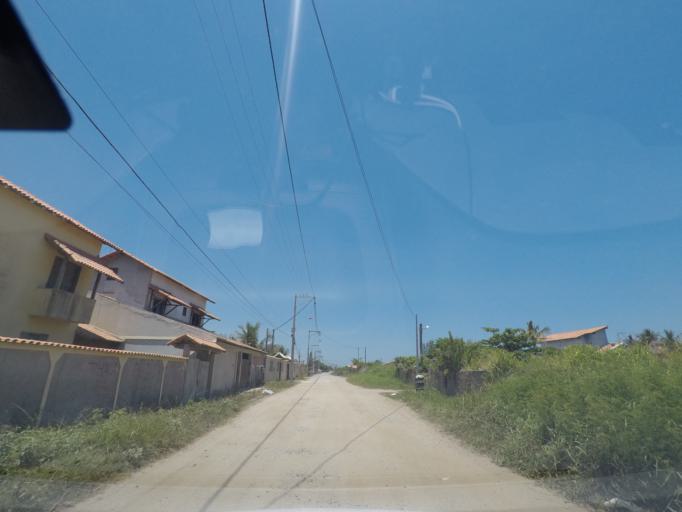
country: BR
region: Rio de Janeiro
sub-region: Niteroi
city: Niteroi
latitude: -22.9681
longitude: -42.9814
